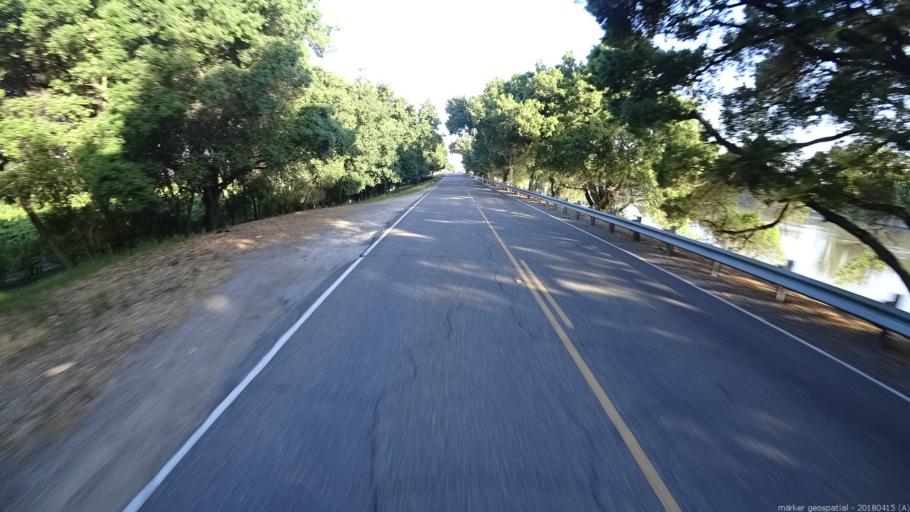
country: US
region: California
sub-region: Sacramento County
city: Walnut Grove
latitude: 38.2603
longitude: -121.5222
